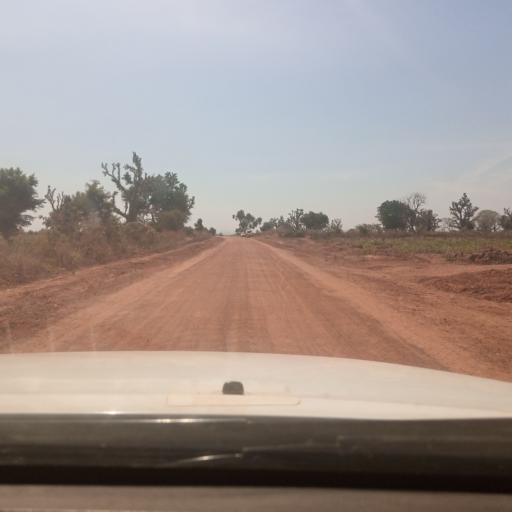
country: NG
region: Adamawa
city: Yola
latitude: 9.1828
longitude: 12.7489
